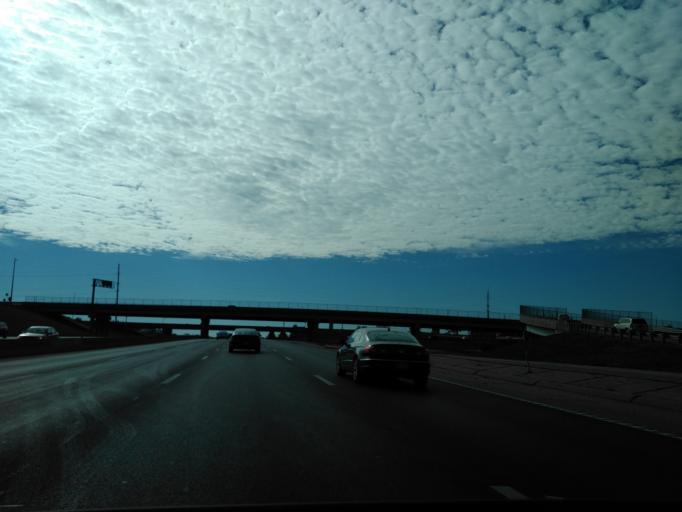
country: US
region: Missouri
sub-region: Saint Louis County
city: Town and Country
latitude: 38.6053
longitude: -90.4510
